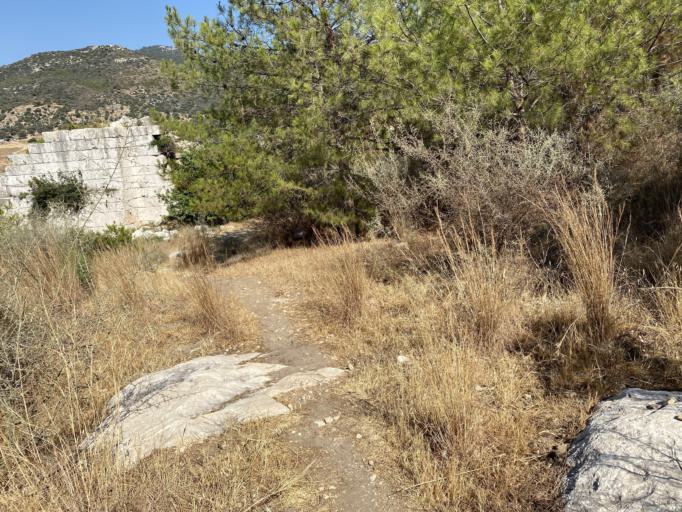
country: TR
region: Antalya
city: Kalkan
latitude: 36.2604
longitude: 29.3135
